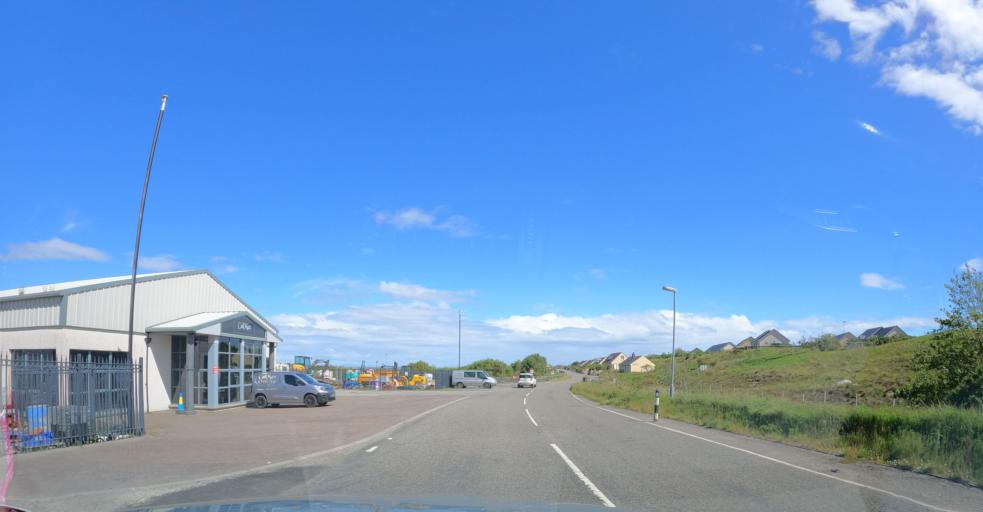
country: GB
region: Scotland
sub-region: Eilean Siar
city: Isle of Lewis
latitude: 58.2482
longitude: -6.4009
